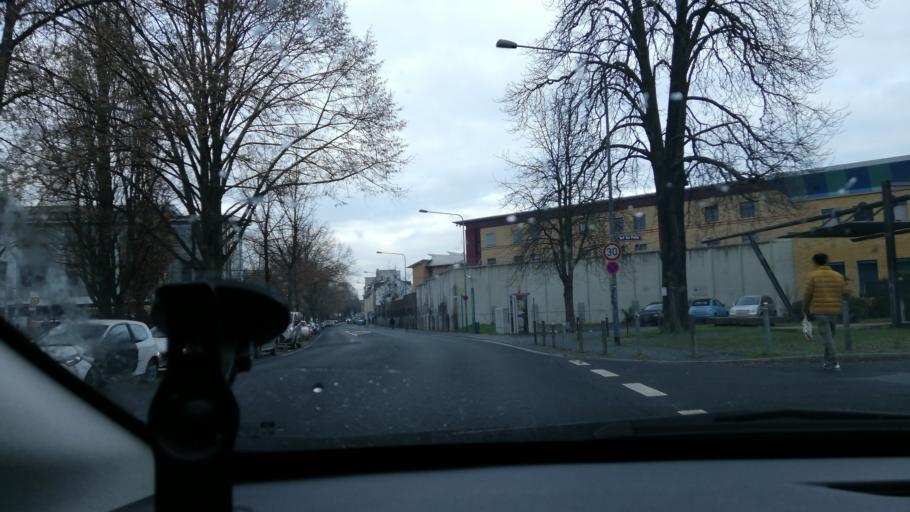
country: DE
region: Hesse
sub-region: Regierungsbezirk Darmstadt
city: Frankfurt am Main
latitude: 50.1485
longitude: 8.6920
